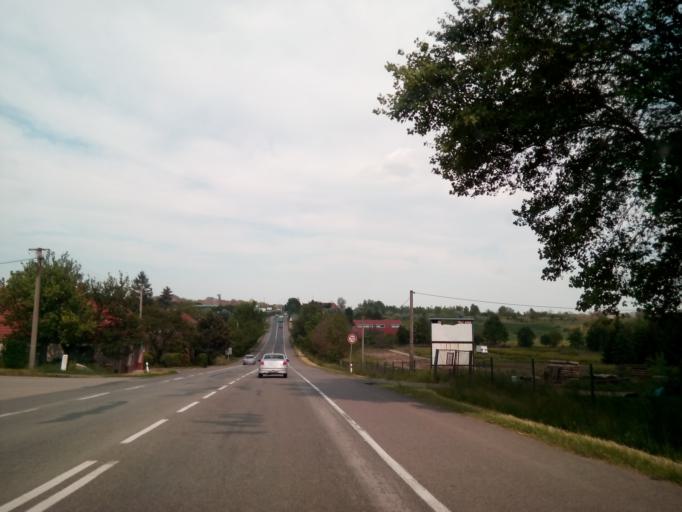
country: CZ
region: South Moravian
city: Tvarozna
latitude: 49.1836
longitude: 16.7521
